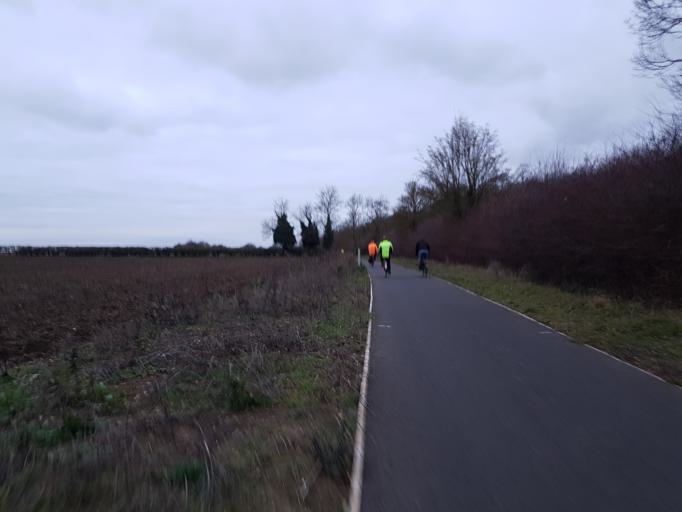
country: GB
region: England
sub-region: Cambridgeshire
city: Bottisham
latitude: 52.2339
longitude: 0.2400
